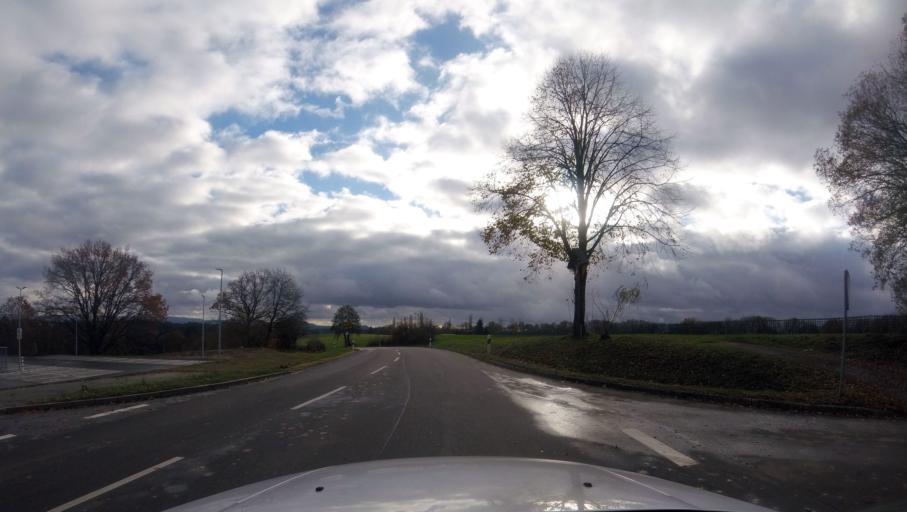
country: DE
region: Baden-Wuerttemberg
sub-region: Regierungsbezirk Stuttgart
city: Spraitbach
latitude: 48.8753
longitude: 9.7608
